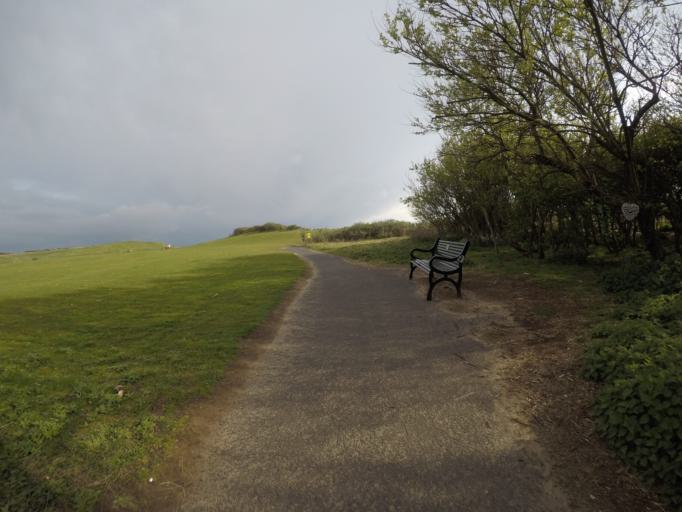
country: GB
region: Scotland
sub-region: North Ayrshire
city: Irvine
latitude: 55.6047
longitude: -4.6912
